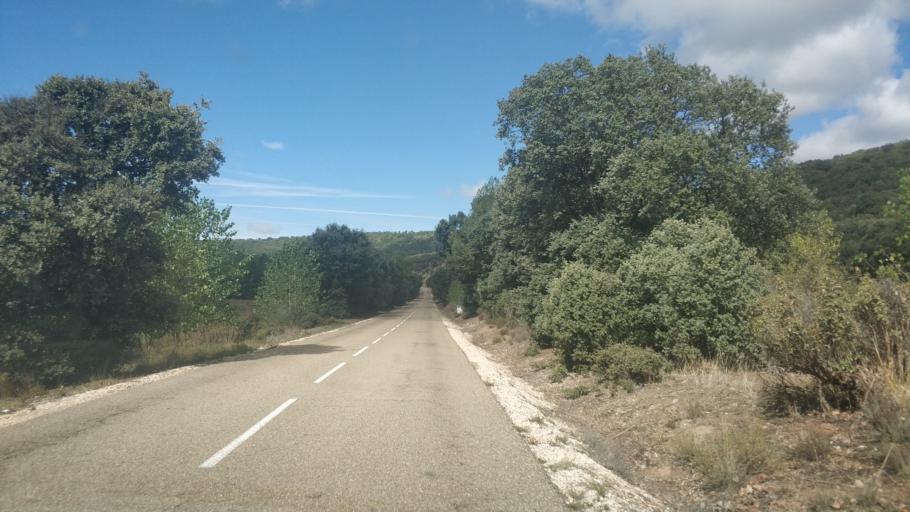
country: ES
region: Castille and Leon
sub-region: Provincia de Burgos
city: Retuerta
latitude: 42.0390
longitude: -3.4858
